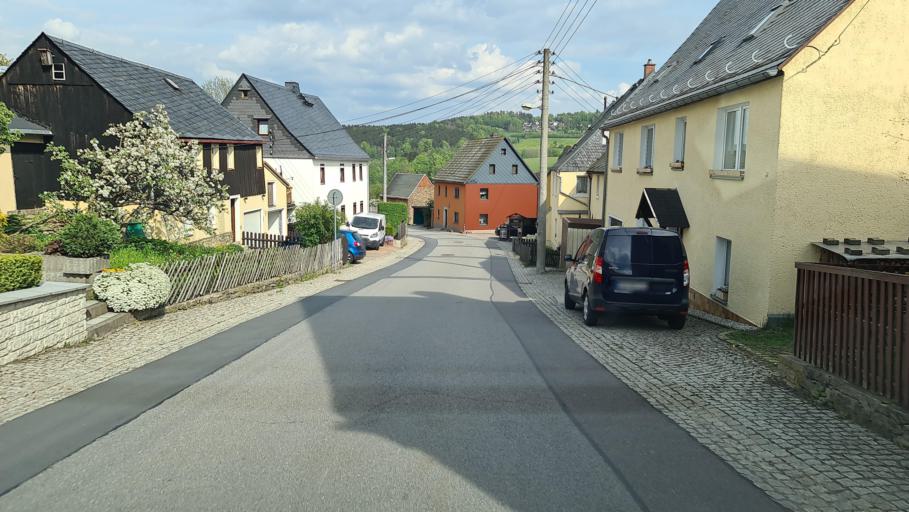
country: DE
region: Saxony
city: Schwarzenberg
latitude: 50.5203
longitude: 12.7787
